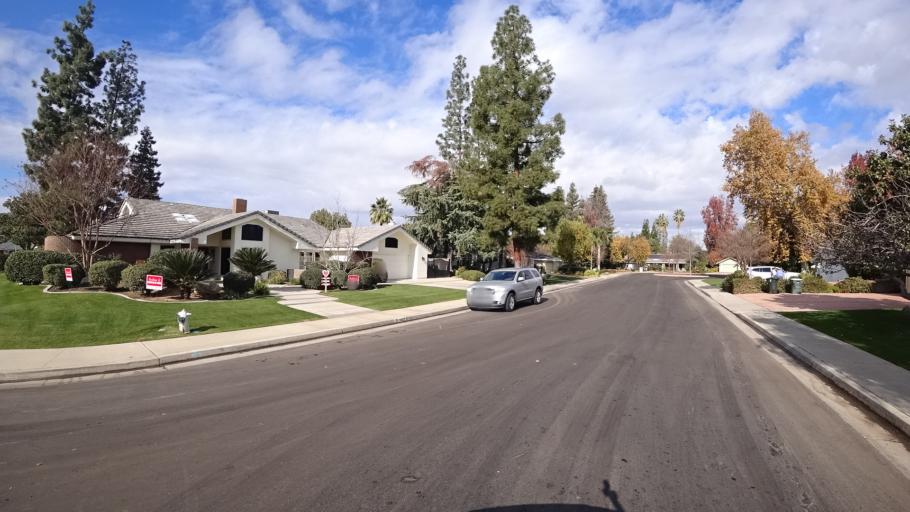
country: US
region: California
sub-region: Kern County
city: Greenacres
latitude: 35.3418
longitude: -119.0902
